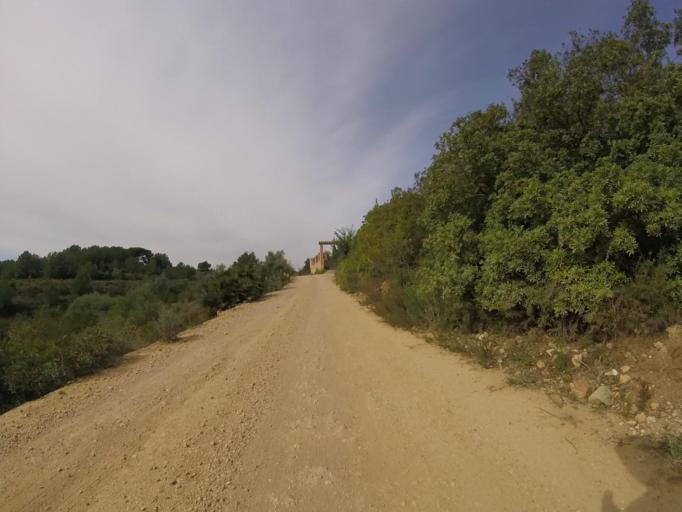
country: ES
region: Valencia
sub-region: Provincia de Castello
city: Torreblanca
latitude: 40.2049
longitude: 0.1464
